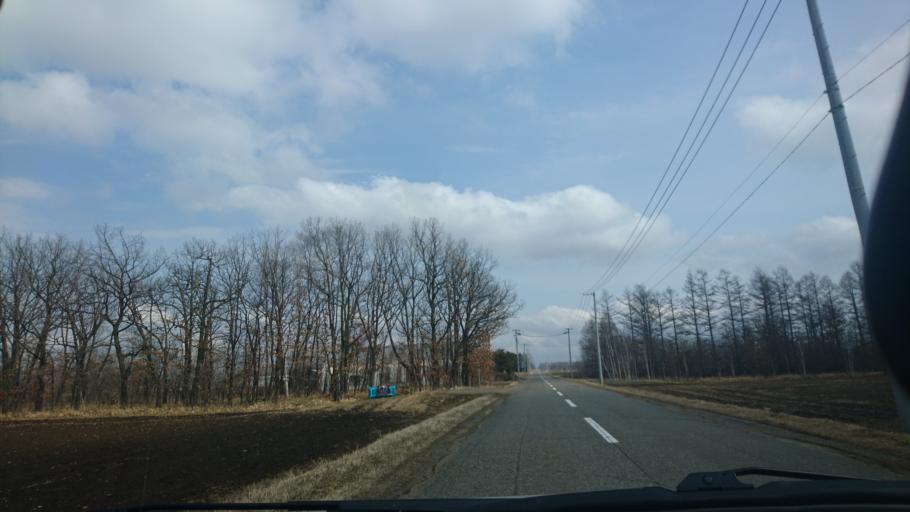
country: JP
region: Hokkaido
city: Otofuke
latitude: 43.2075
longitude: 143.2702
